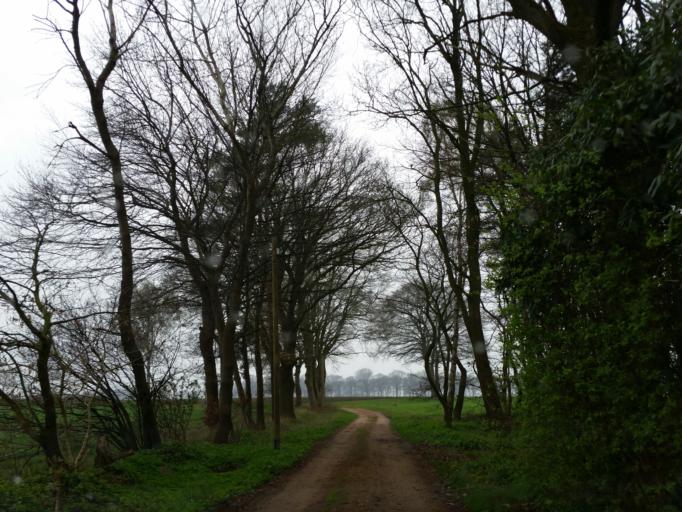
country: DE
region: Lower Saxony
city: Hipstedt
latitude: 53.5724
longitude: 8.9781
